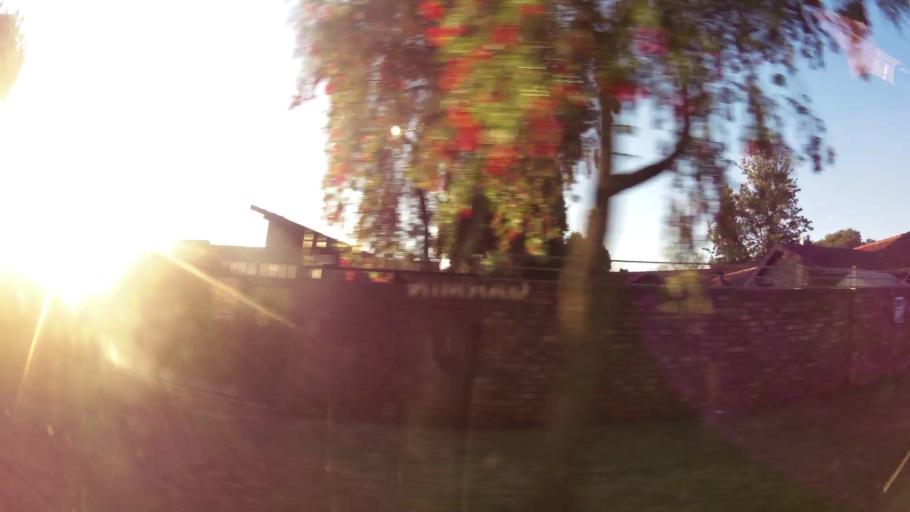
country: ZA
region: Gauteng
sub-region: City of Tshwane Metropolitan Municipality
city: Centurion
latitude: -25.8726
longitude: 28.1484
